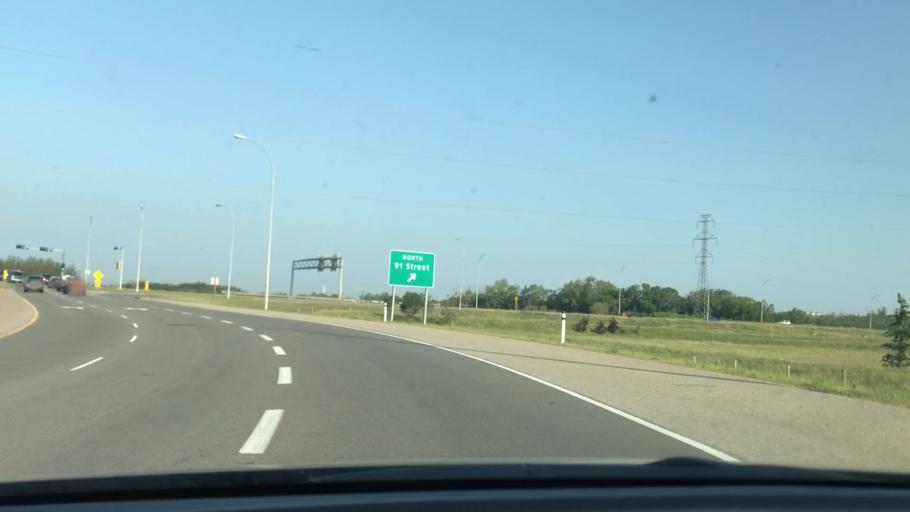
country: CA
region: Alberta
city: Beaumont
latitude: 53.4397
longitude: -113.4642
